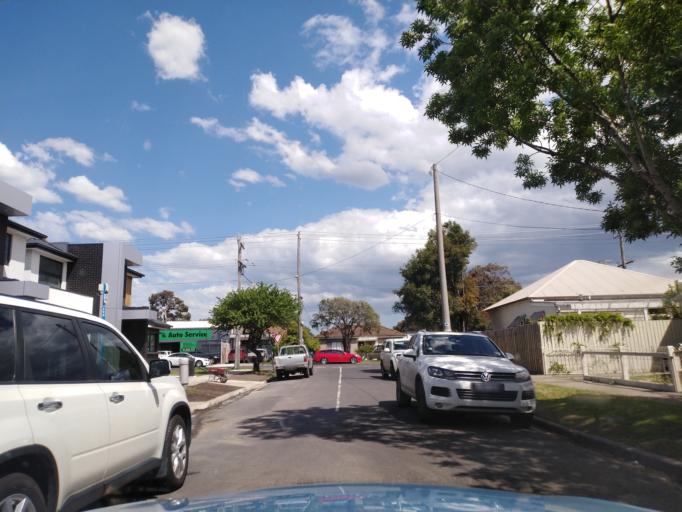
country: AU
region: Victoria
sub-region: Hobsons Bay
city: South Kingsville
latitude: -37.8330
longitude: 144.8693
